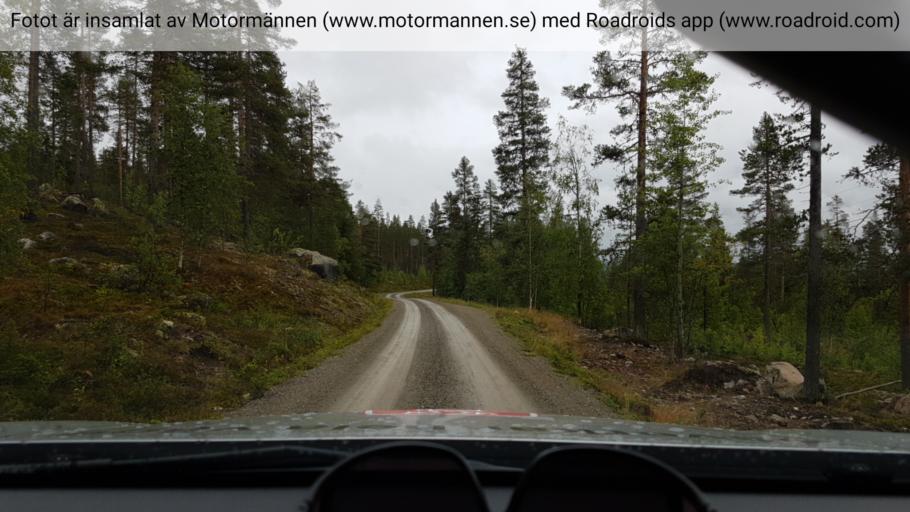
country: SE
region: Vaesterbotten
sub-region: Storumans Kommun
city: Storuman
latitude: 64.8329
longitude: 17.4047
